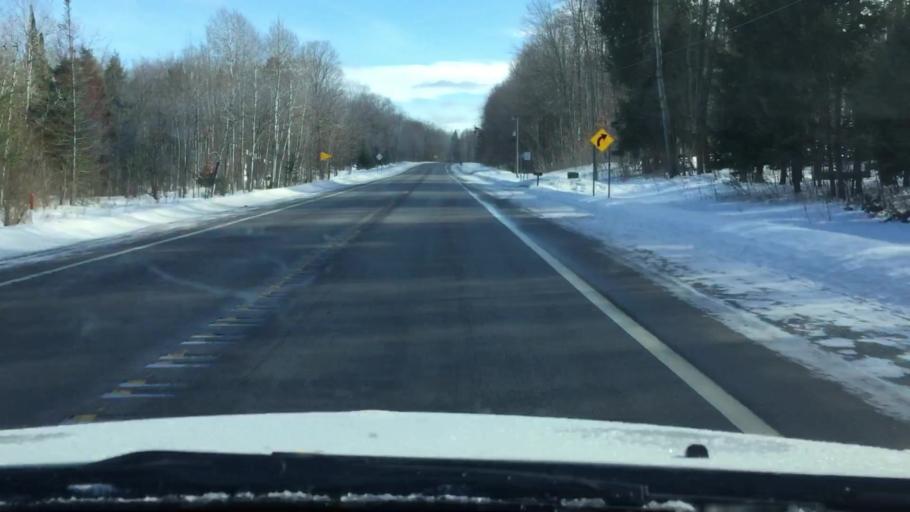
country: US
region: Michigan
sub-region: Antrim County
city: Mancelona
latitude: 44.9887
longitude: -85.0592
